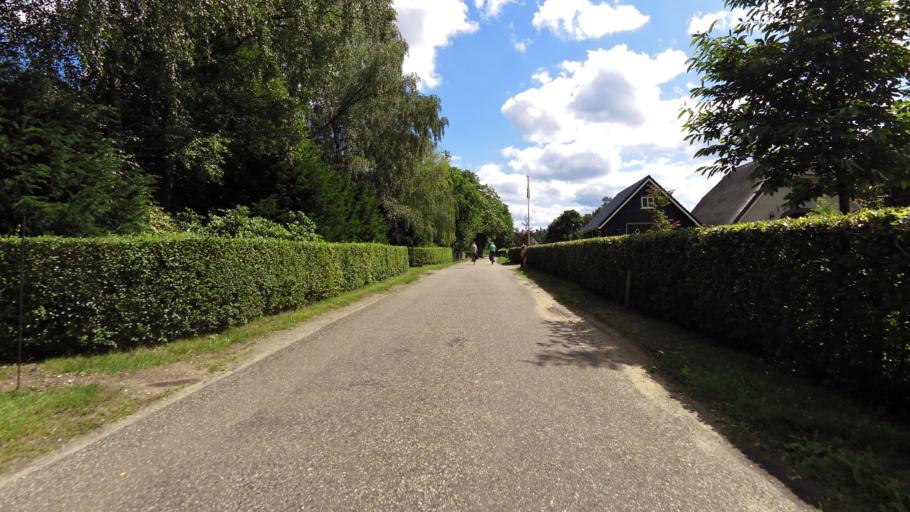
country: NL
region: Gelderland
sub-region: Gemeente Epe
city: Vaassen
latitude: 52.2516
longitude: 5.9407
